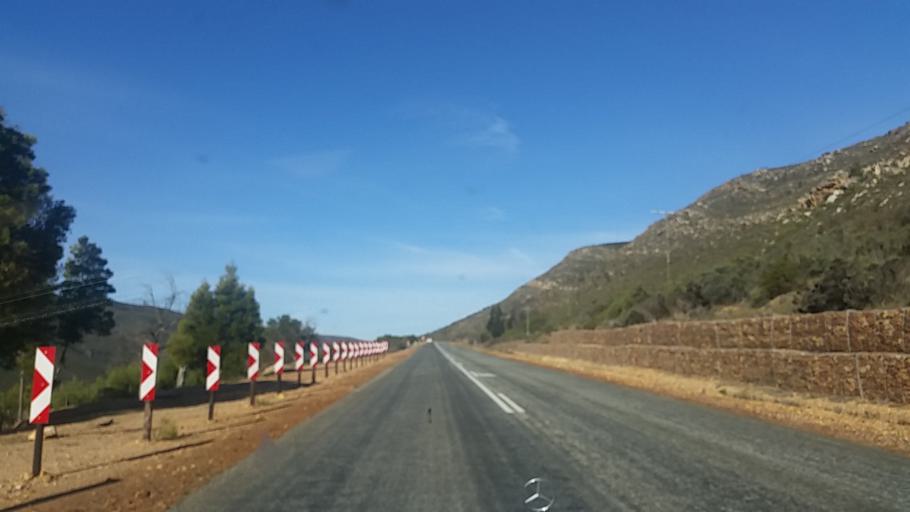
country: ZA
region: Western Cape
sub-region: Eden District Municipality
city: Knysna
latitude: -33.7488
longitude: 22.9726
